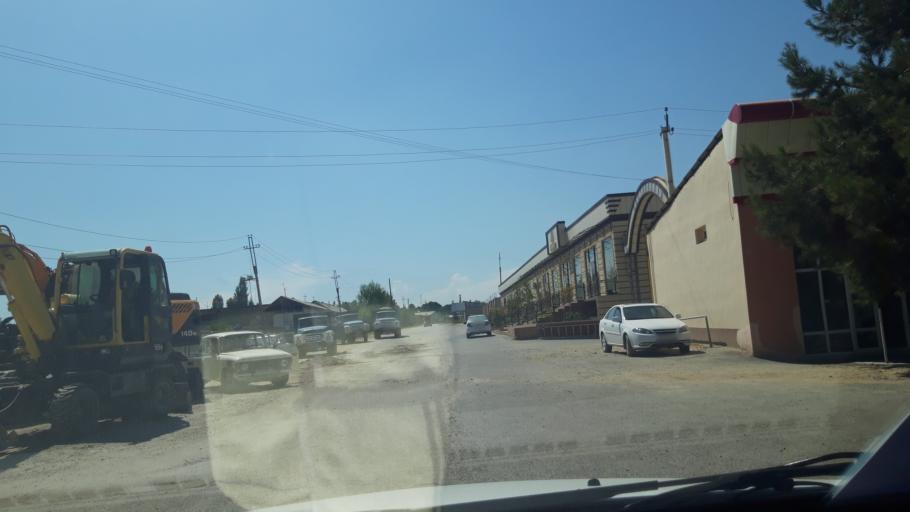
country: UZ
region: Namangan
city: Namangan
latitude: 41.0399
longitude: 71.6966
